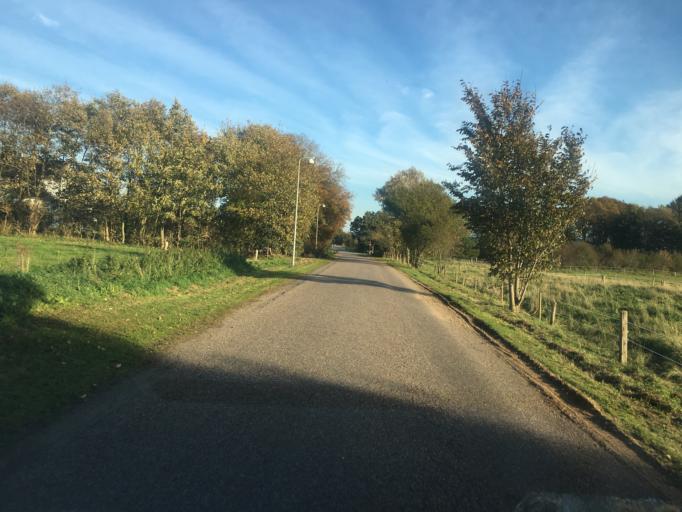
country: DK
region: South Denmark
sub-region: Tonder Kommune
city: Tonder
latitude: 54.9152
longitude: 8.9099
